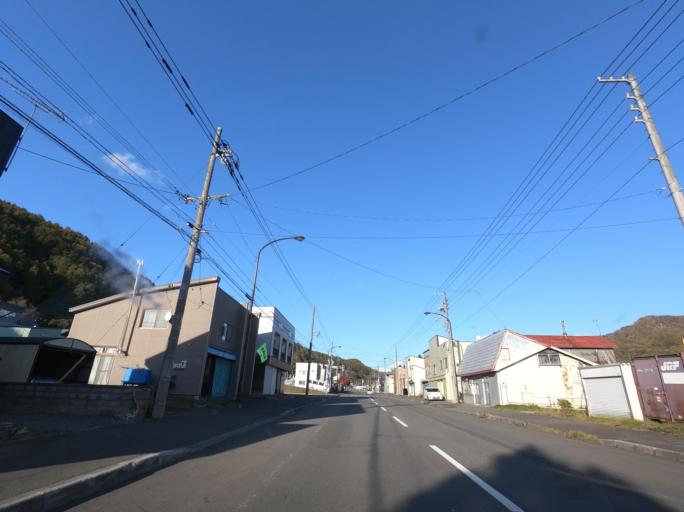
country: JP
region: Hokkaido
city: Iwamizawa
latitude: 43.0483
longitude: 141.9648
